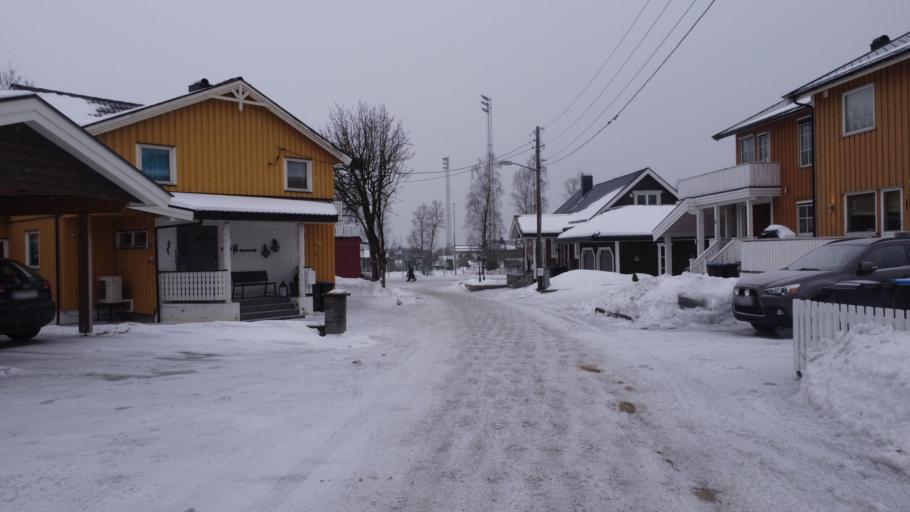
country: NO
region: Nordland
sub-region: Rana
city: Mo i Rana
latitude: 66.3127
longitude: 14.1533
